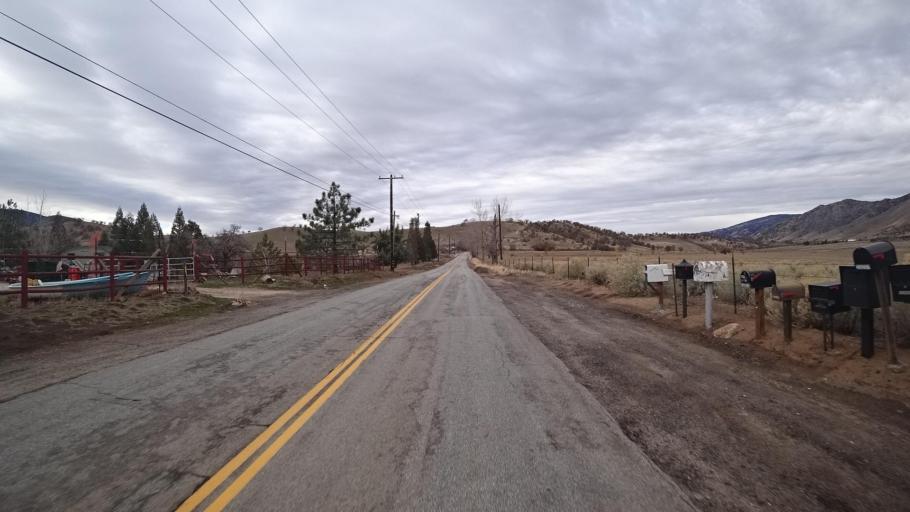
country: US
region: California
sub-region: Kern County
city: Golden Hills
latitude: 35.1179
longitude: -118.5452
